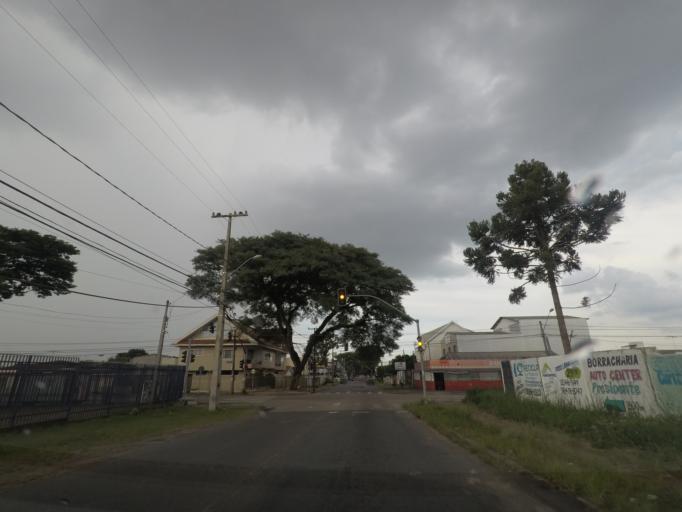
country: BR
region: Parana
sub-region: Curitiba
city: Curitiba
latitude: -25.4794
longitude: -49.2570
